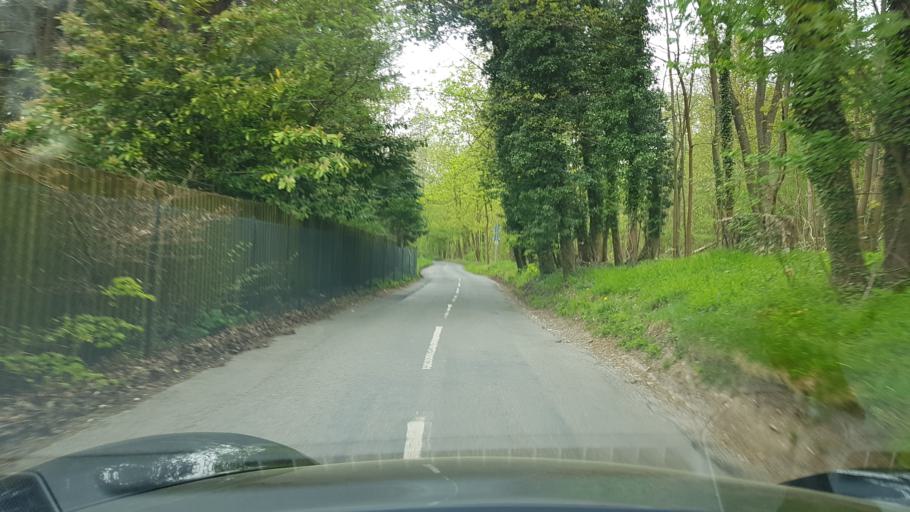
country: GB
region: England
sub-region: Surrey
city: East Horsley
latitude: 51.2484
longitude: -0.4335
